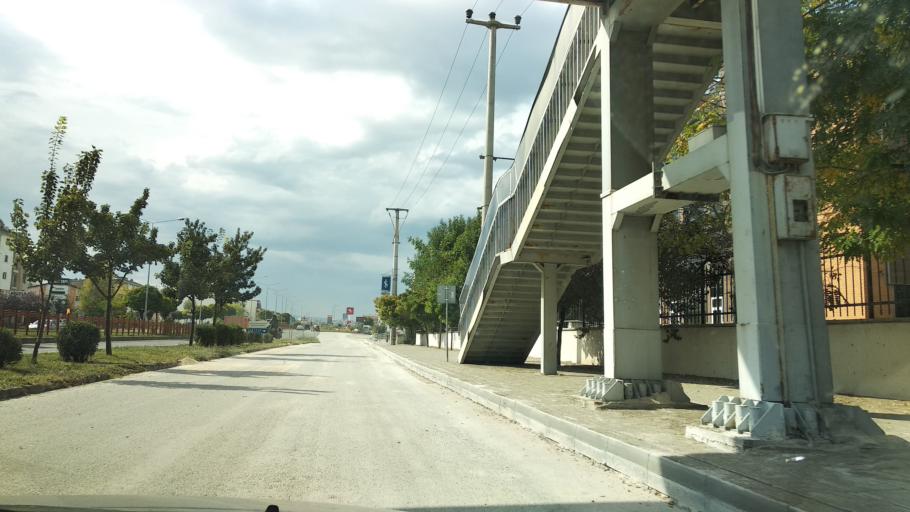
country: TR
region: Bolu
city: Bolu
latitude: 40.7382
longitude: 31.6023
